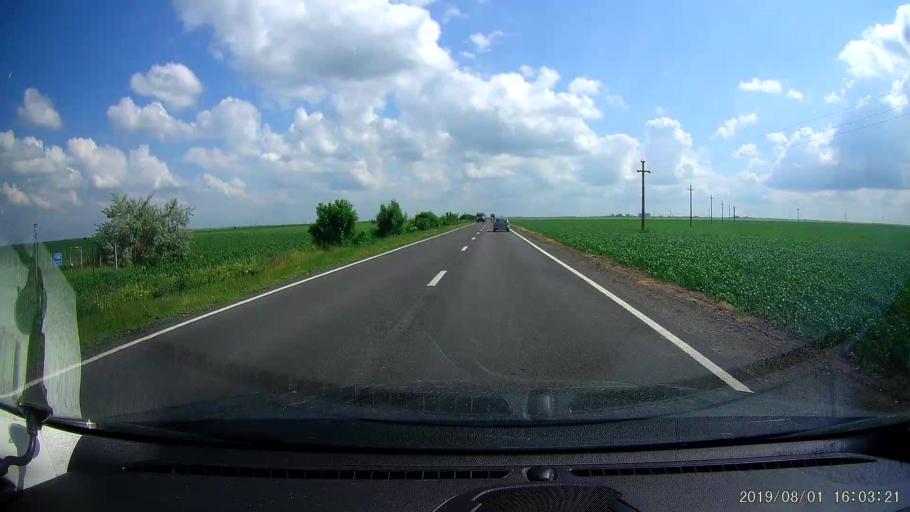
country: RO
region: Calarasi
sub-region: Comuna Dragalina
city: Drajna Noua
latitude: 44.4732
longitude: 27.3843
